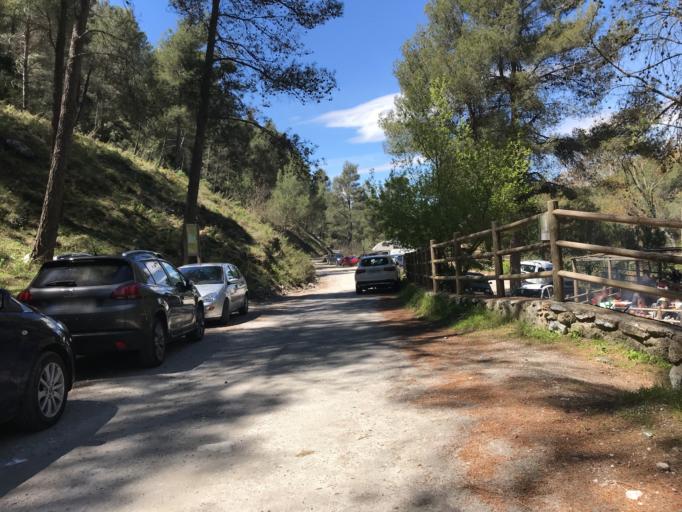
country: ES
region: Andalusia
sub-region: Provincia de Malaga
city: Alcaucin
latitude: 36.9153
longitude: -4.0920
